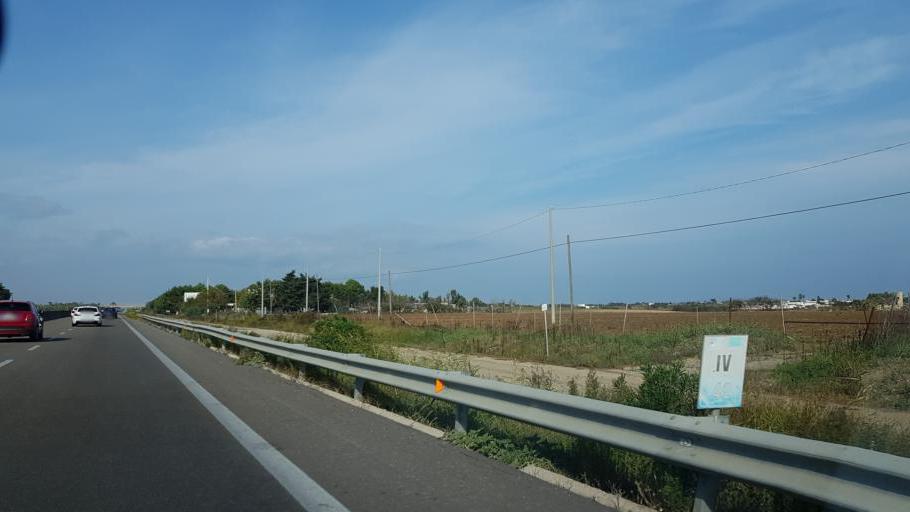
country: IT
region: Apulia
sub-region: Provincia di Brindisi
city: Brindisi
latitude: 40.6840
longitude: 17.8339
